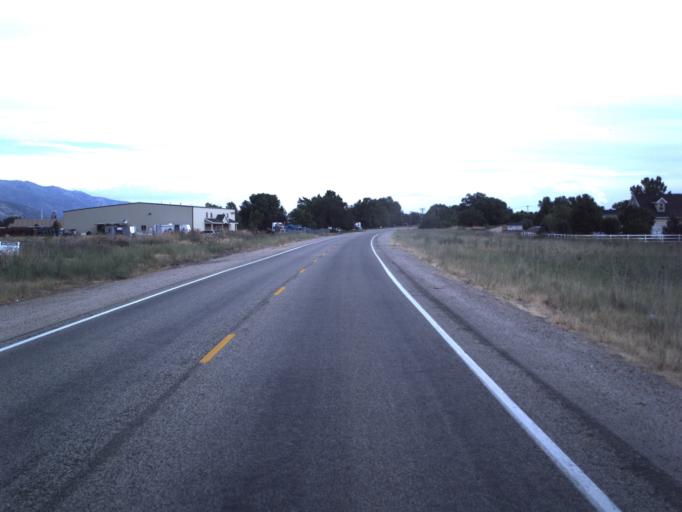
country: US
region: Utah
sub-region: Weber County
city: Farr West
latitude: 41.3168
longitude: -112.0284
